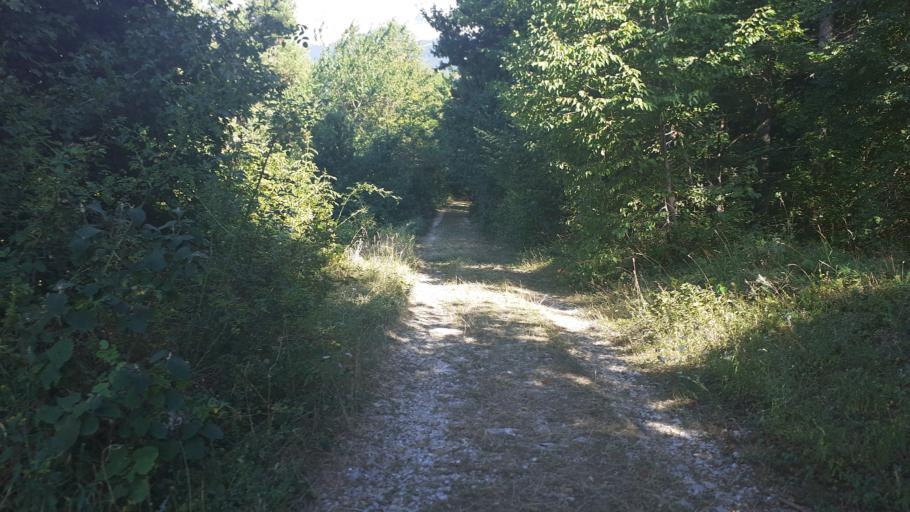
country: IT
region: Abruzzo
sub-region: Provincia di Pescara
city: Sant'Eufemia a Maiella
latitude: 42.1049
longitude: 14.0061
